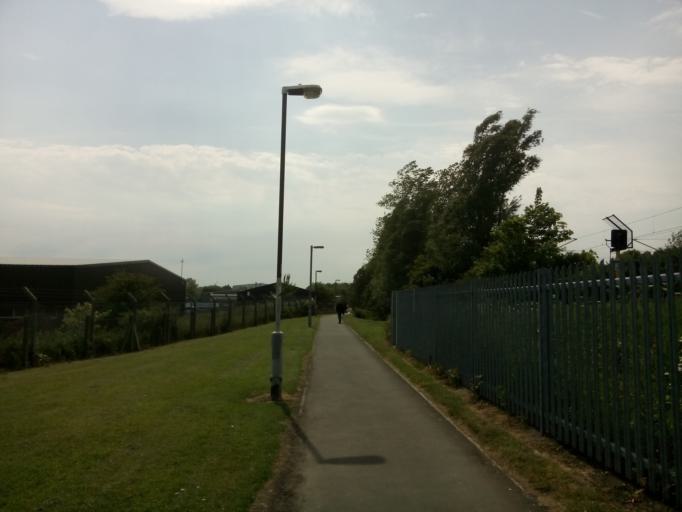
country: GB
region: England
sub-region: Northumberland
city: Backworth
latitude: 55.0233
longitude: -1.5418
